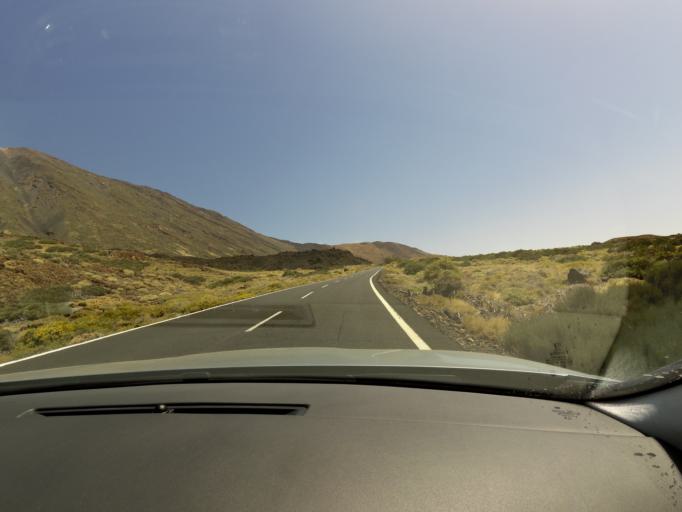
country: ES
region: Canary Islands
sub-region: Provincia de Santa Cruz de Tenerife
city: Vilaflor
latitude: 28.2438
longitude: -16.6302
